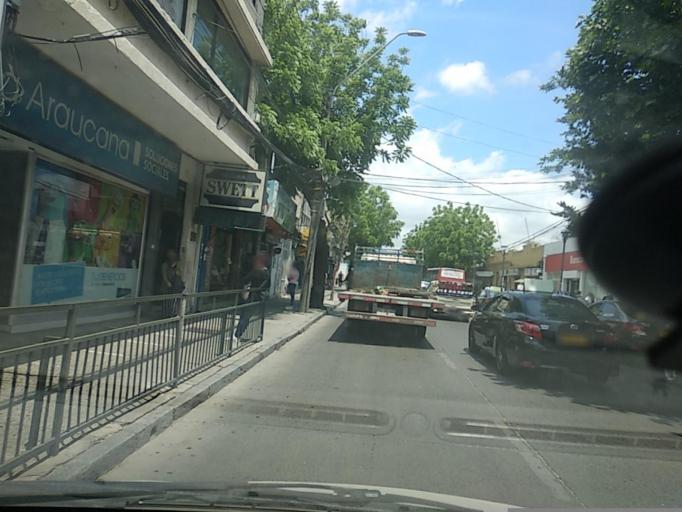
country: CL
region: Valparaiso
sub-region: Provincia de Marga Marga
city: Quilpue
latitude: -33.0471
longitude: -71.4420
